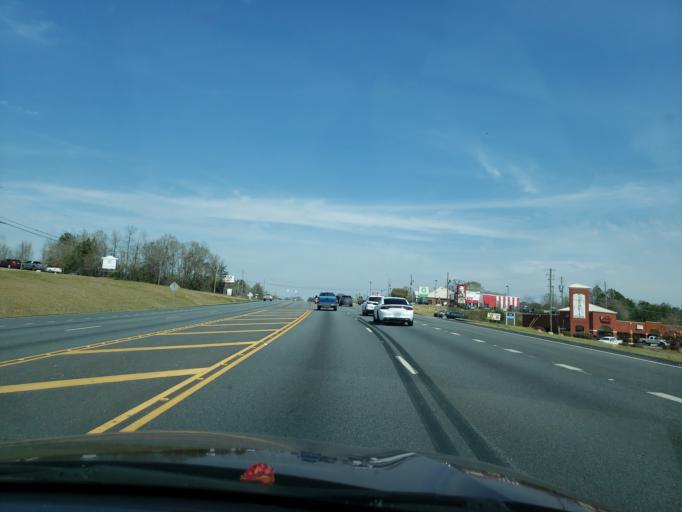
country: US
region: Alabama
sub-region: Elmore County
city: Millbrook
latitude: 32.5085
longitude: -86.3824
